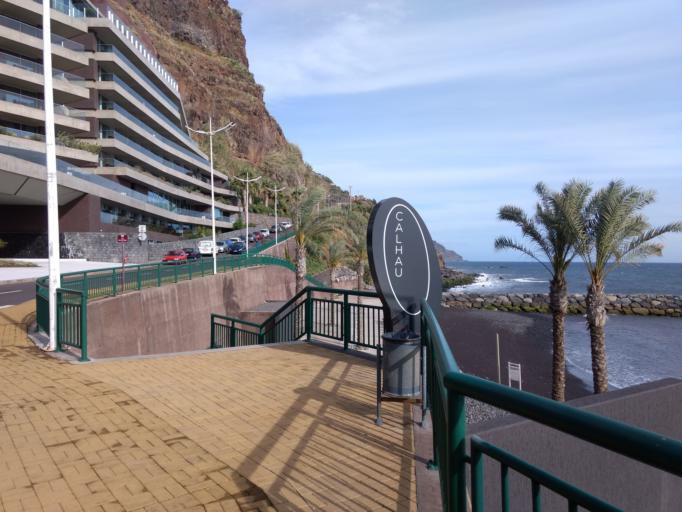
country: PT
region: Madeira
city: Calheta
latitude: 32.7166
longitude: -17.1688
